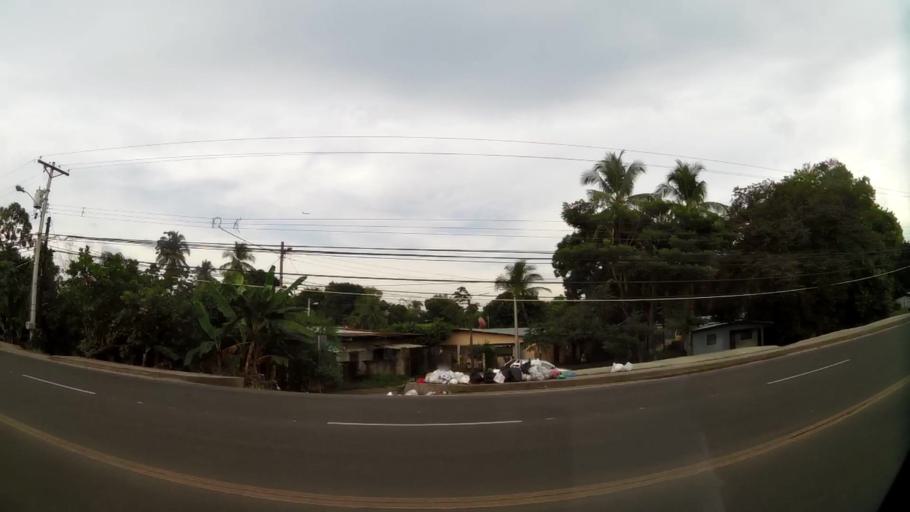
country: PA
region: Panama
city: Tocumen
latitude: 9.0937
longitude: -79.3670
